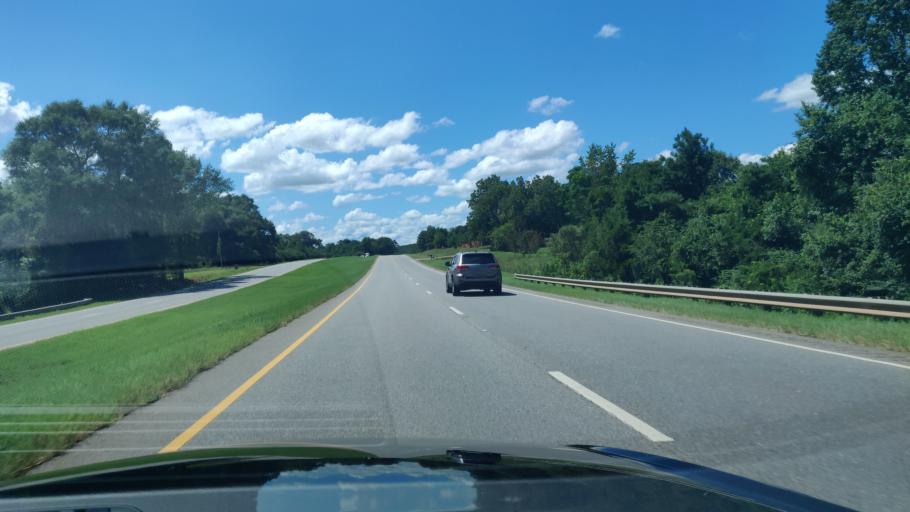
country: US
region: Georgia
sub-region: Terrell County
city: Dawson
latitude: 31.9051
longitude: -84.5251
